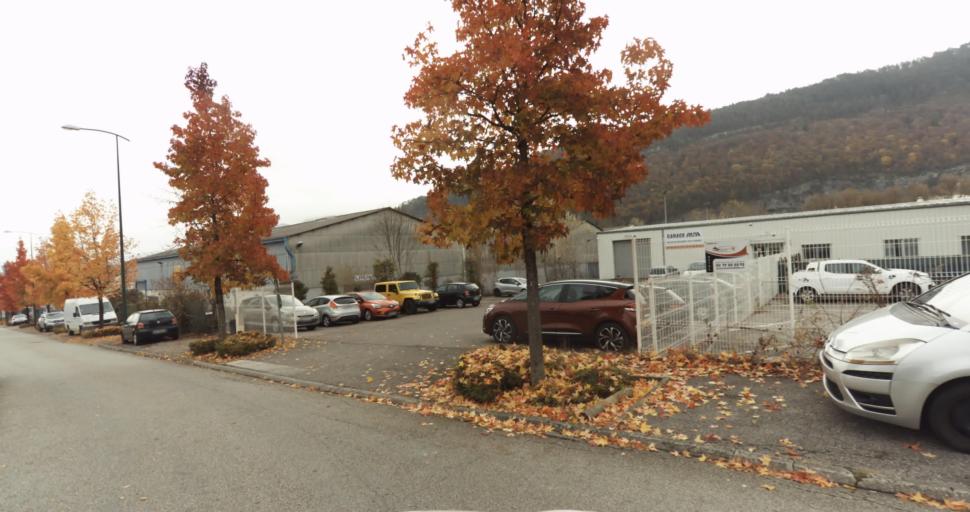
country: FR
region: Rhone-Alpes
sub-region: Departement de la Haute-Savoie
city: Annecy
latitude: 45.8848
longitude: 6.1122
